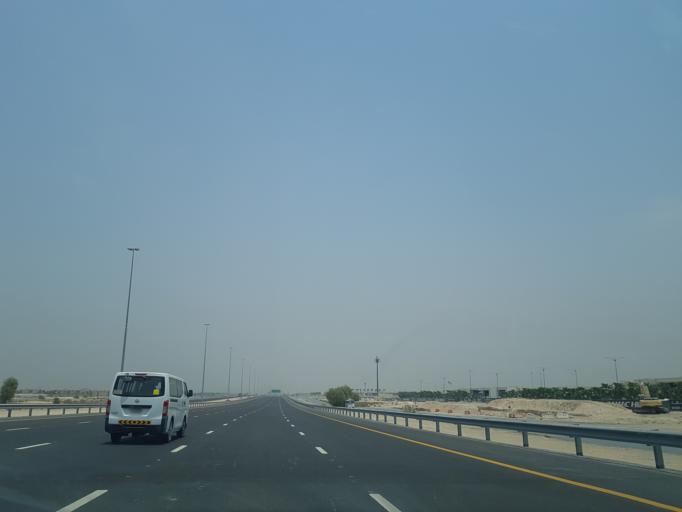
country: AE
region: Dubai
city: Dubai
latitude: 25.0268
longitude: 55.2449
